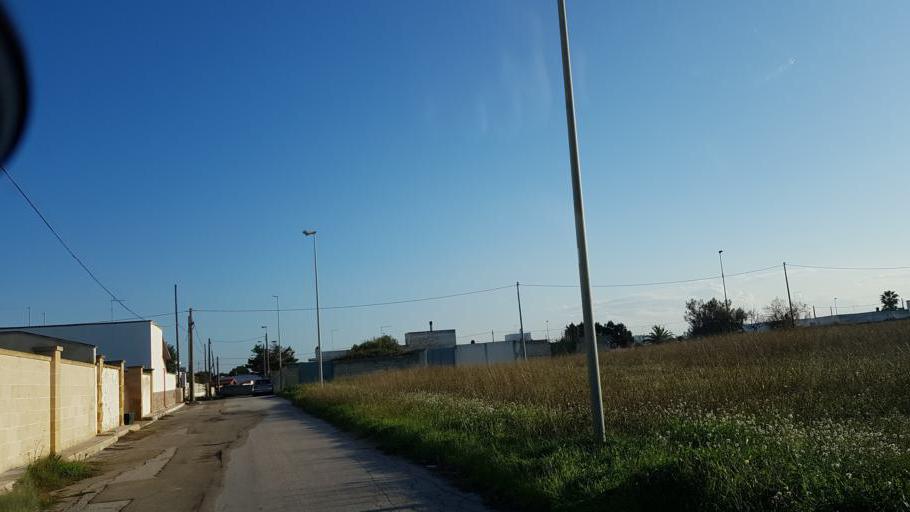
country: IT
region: Apulia
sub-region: Provincia di Brindisi
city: Torchiarolo
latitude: 40.5151
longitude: 18.0945
